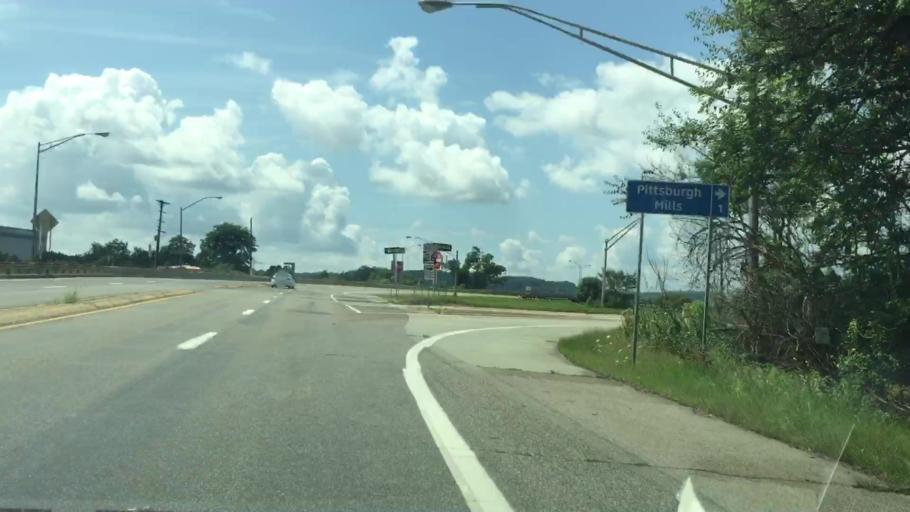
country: US
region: Pennsylvania
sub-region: Allegheny County
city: Cheswick
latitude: 40.5555
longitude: -79.8088
